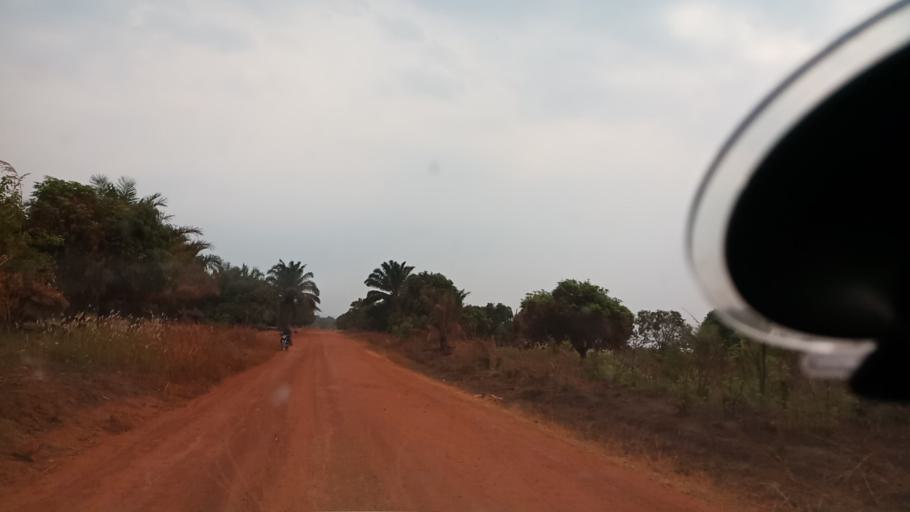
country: ZM
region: Luapula
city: Nchelenge
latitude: -9.1400
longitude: 28.2945
